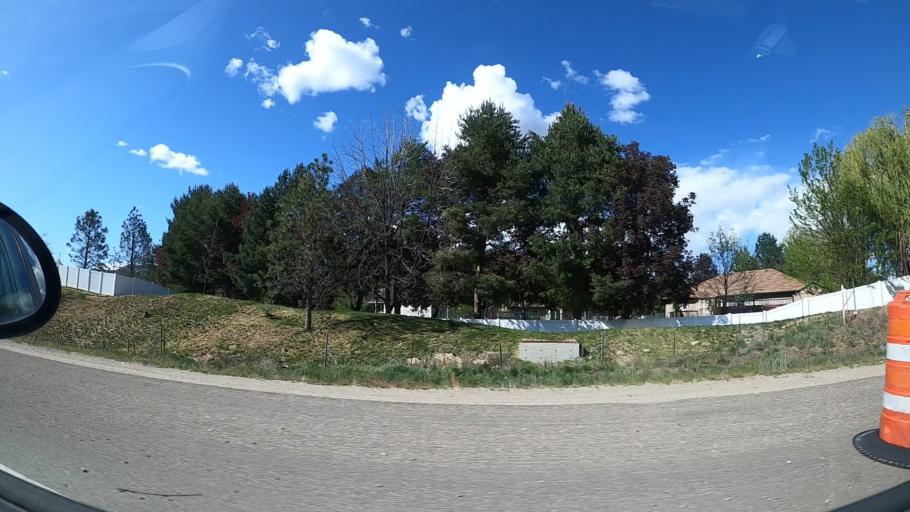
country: US
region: Idaho
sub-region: Ada County
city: Eagle
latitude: 43.6922
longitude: -116.3614
